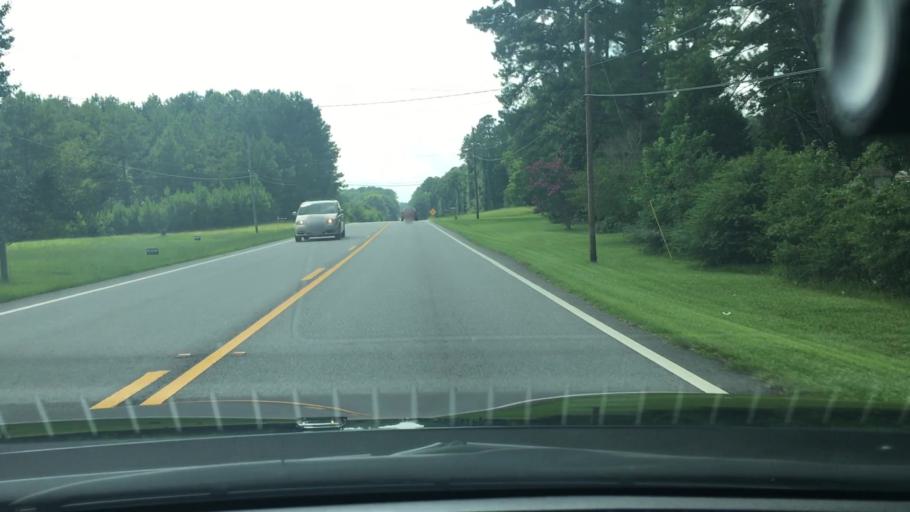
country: US
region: Georgia
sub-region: Coweta County
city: East Newnan
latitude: 33.3326
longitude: -84.7073
